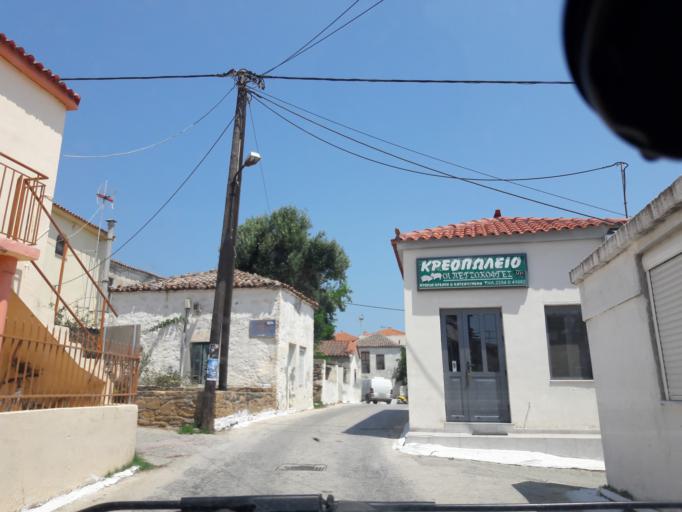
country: GR
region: North Aegean
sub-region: Nomos Lesvou
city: Myrina
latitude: 39.9266
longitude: 25.3329
